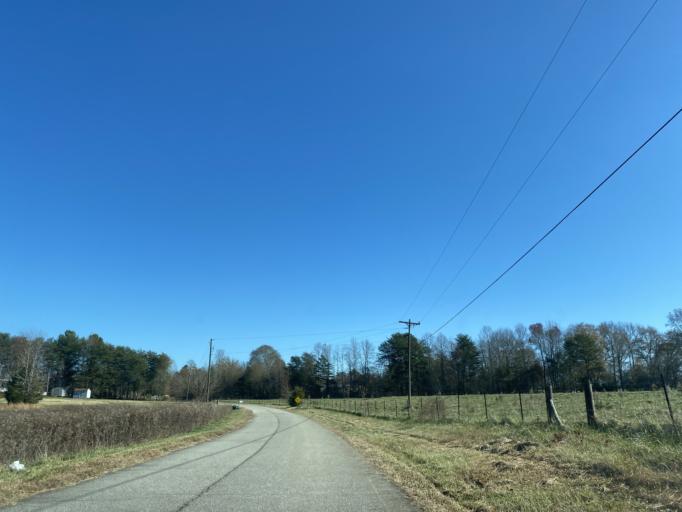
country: US
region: South Carolina
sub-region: Spartanburg County
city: Mayo
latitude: 35.1458
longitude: -81.7751
